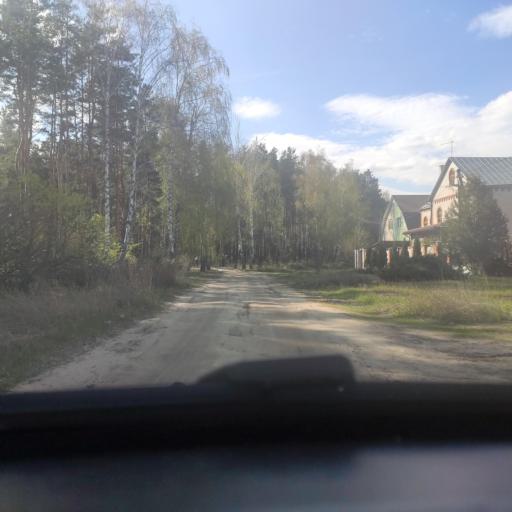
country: RU
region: Voronezj
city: Somovo
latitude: 51.7496
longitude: 39.3245
